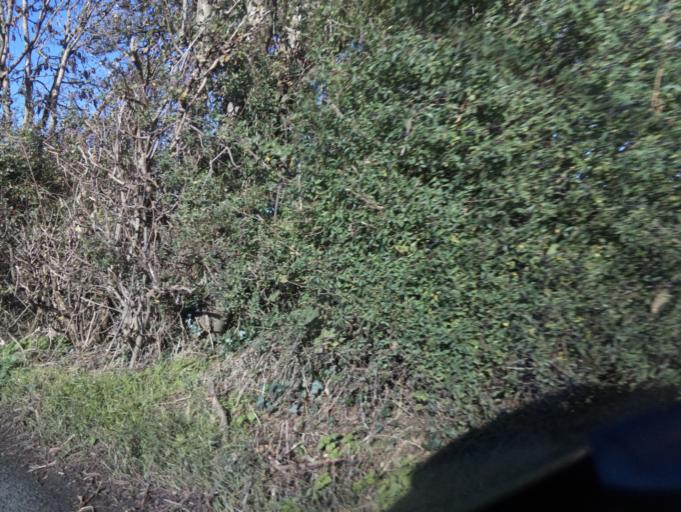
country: GB
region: England
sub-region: Somerset
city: Ilchester
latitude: 50.9701
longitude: -2.7023
